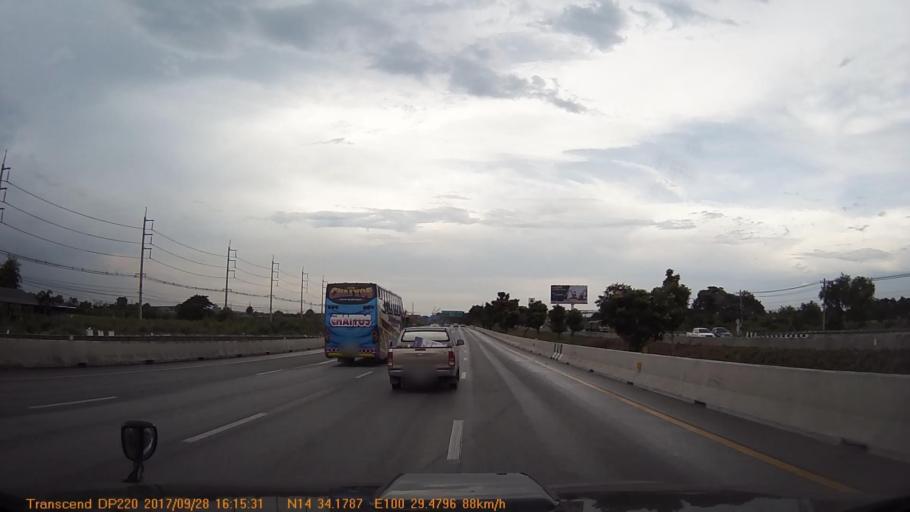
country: TH
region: Ang Thong
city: Ang Thong
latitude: 14.5701
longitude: 100.4910
